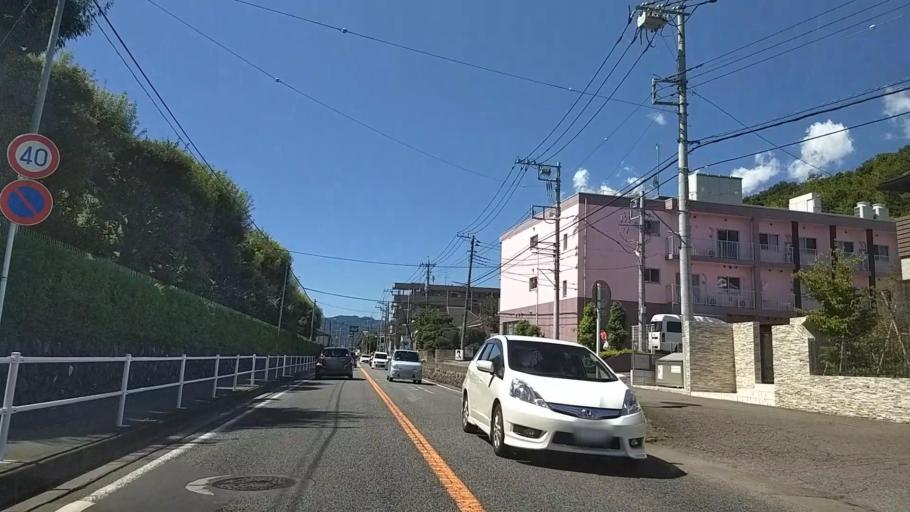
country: JP
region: Tokyo
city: Hachioji
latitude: 35.5917
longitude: 139.2962
